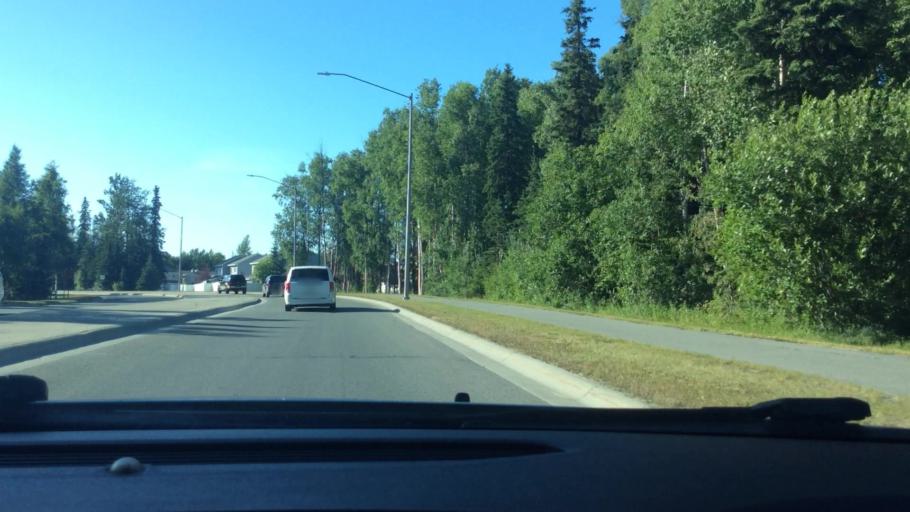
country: US
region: Alaska
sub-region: Anchorage Municipality
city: Anchorage
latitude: 61.2322
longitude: -149.7686
